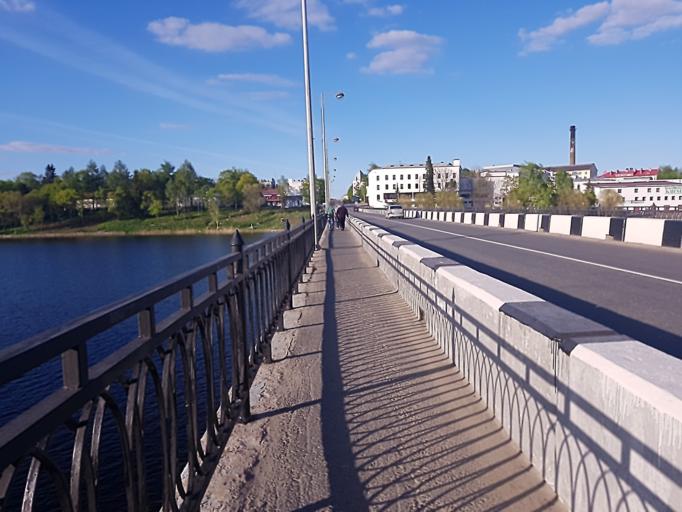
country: RU
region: Republic of Karelia
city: Sortavala
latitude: 61.7000
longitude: 30.6846
